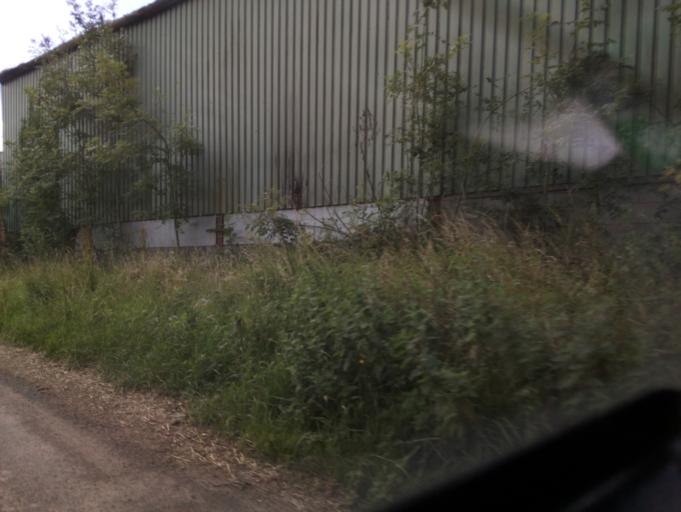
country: GB
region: England
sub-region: Gloucestershire
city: Mitcheldean
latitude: 51.8400
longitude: -2.4297
